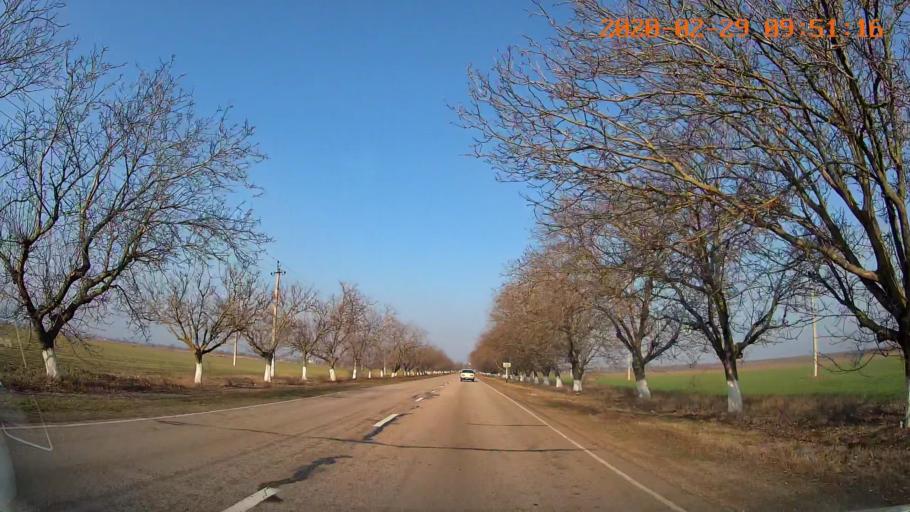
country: MD
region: Telenesti
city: Slobozia
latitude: 46.7072
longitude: 29.7422
